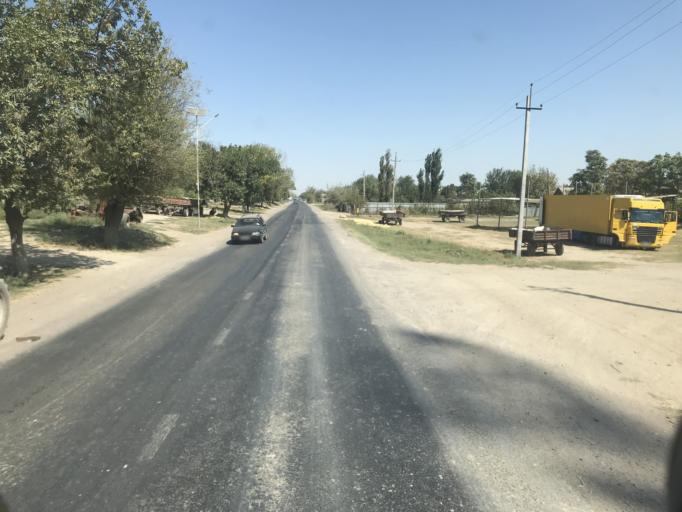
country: KZ
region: Ongtustik Qazaqstan
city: Ilyich
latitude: 40.9278
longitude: 68.4883
